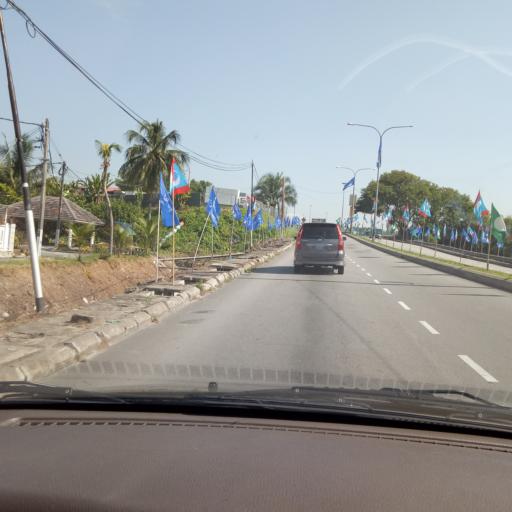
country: MY
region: Selangor
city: Kampong Baharu Balakong
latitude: 3.0286
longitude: 101.7627
